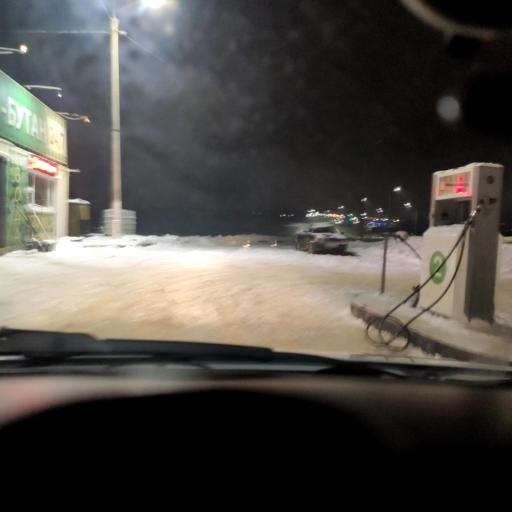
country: RU
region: Voronezj
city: Semiluki
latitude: 51.6498
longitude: 39.0300
